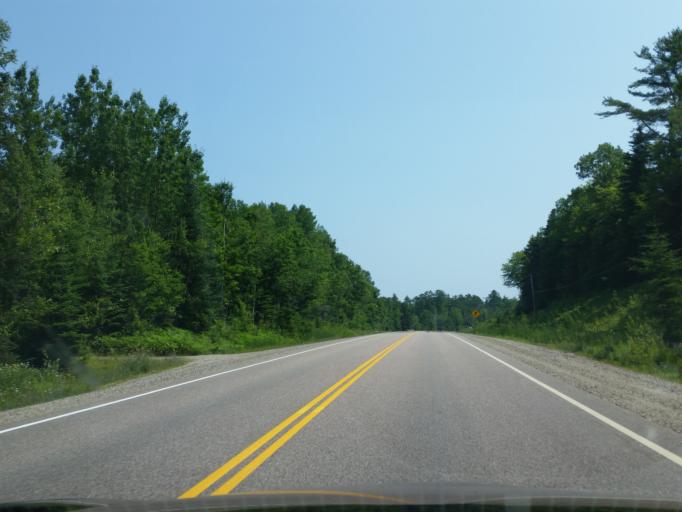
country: CA
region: Ontario
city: Deep River
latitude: 46.1812
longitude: -77.7596
